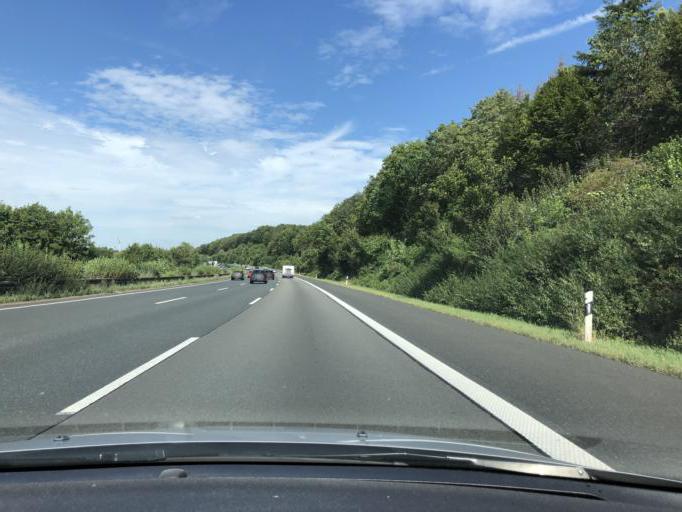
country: DE
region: Lower Saxony
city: Juhnde
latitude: 51.4179
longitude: 9.8395
